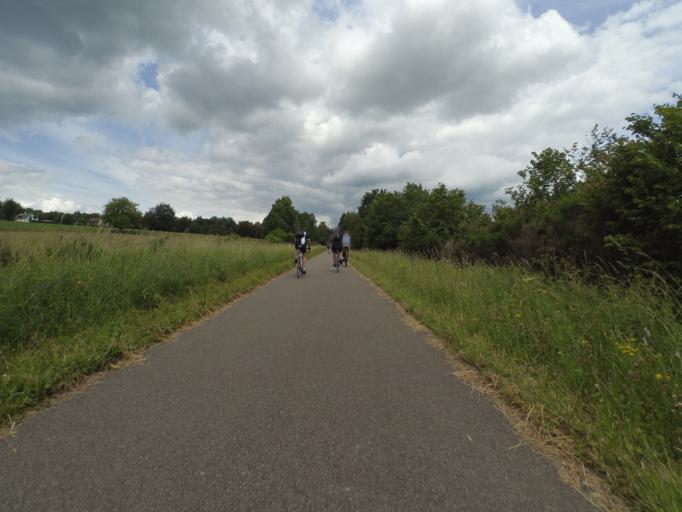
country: DE
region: North Rhine-Westphalia
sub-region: Regierungsbezirk Koln
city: Monschau
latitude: 50.5692
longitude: 6.2362
